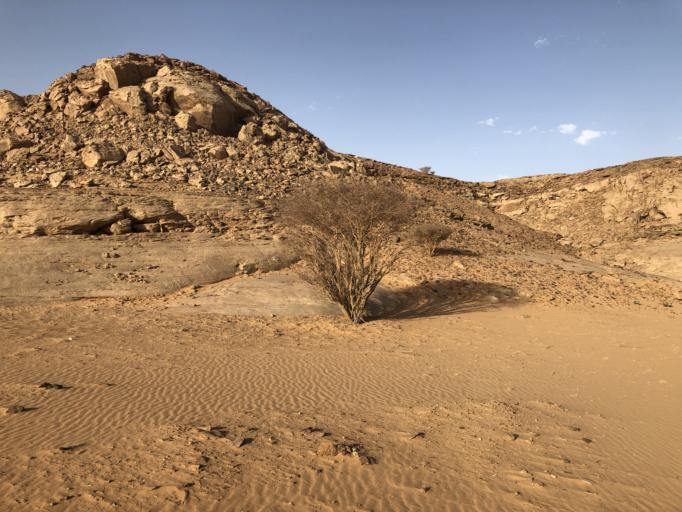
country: SA
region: Ar Riyad
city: shokhaib
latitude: 23.6090
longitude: 46.0790
